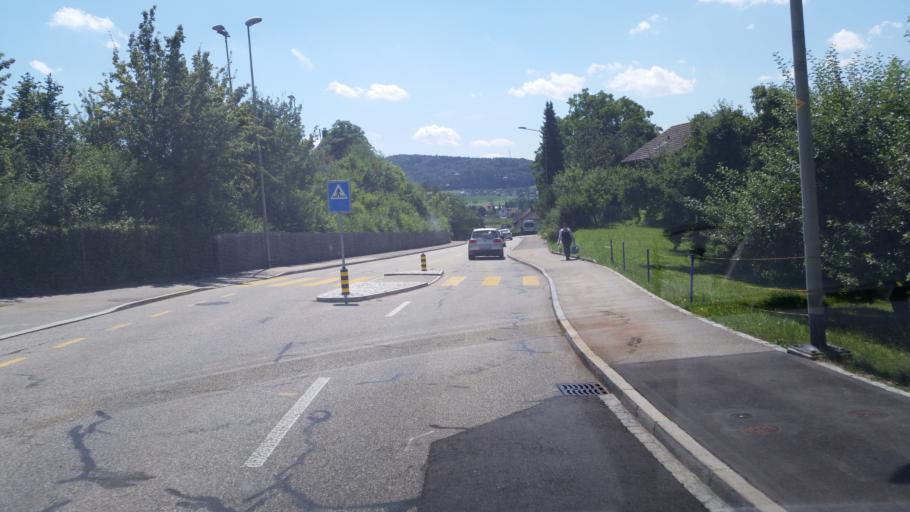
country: CH
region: Zurich
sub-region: Bezirk Dielsdorf
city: Otelfingen
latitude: 47.4640
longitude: 8.3900
